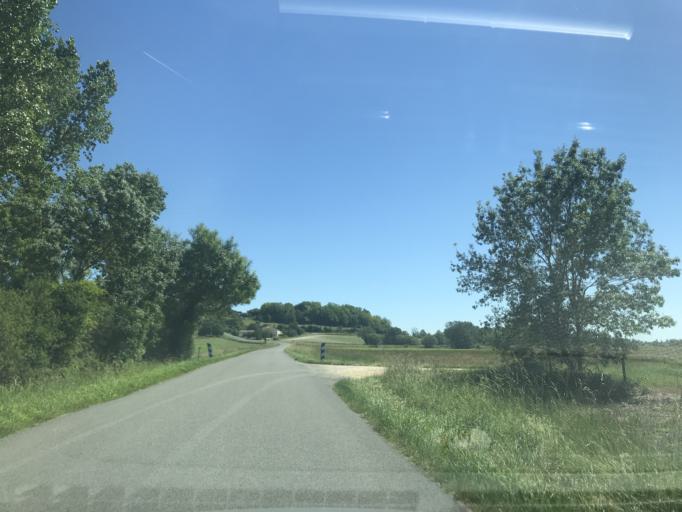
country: FR
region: Poitou-Charentes
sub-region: Departement de la Charente-Maritime
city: Mortagne-sur-Gironde
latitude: 45.3990
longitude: -0.7085
